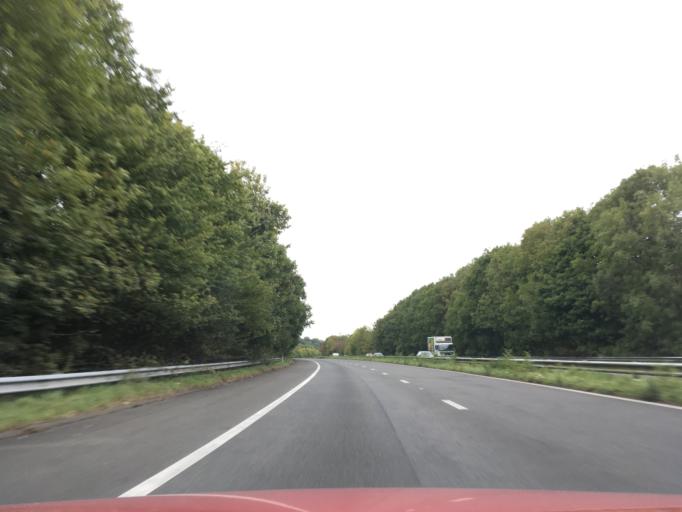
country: GB
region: Wales
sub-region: Monmouthshire
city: Caldicot
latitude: 51.6070
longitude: -2.7378
